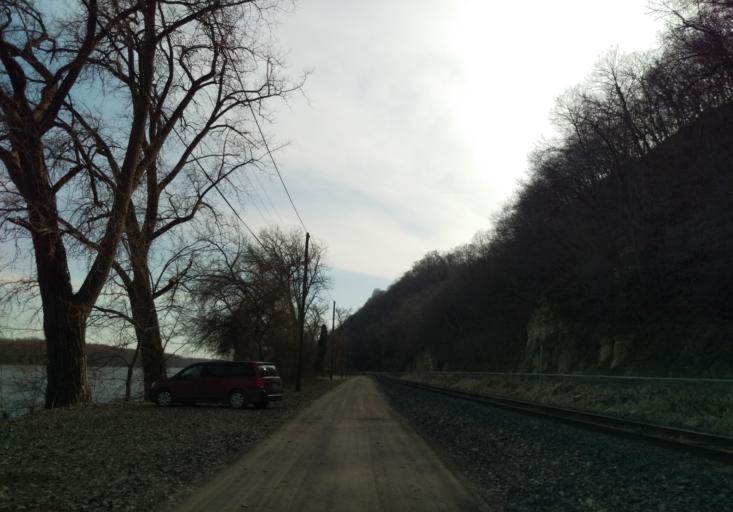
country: US
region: Wisconsin
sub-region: Crawford County
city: Prairie du Chien
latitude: 43.0680
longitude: -91.1802
